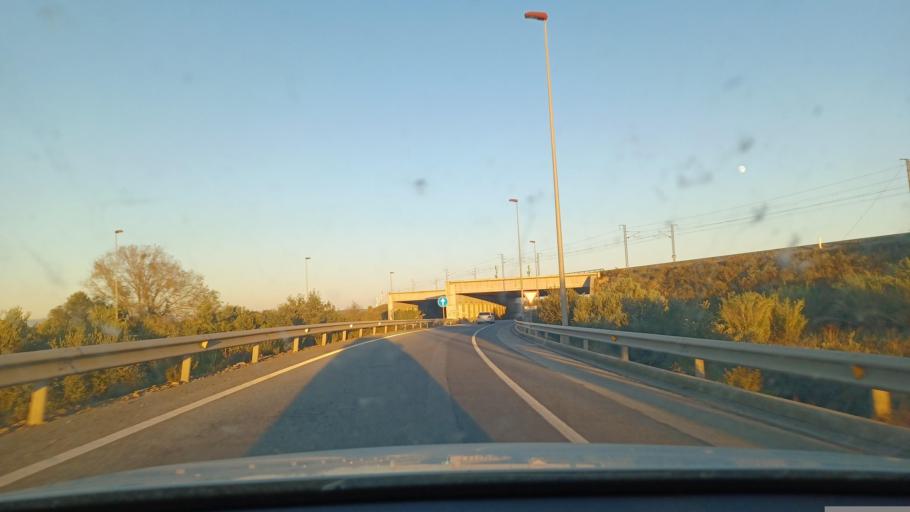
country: ES
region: Catalonia
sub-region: Provincia de Tarragona
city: Vila-seca
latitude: 41.1361
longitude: 1.1500
